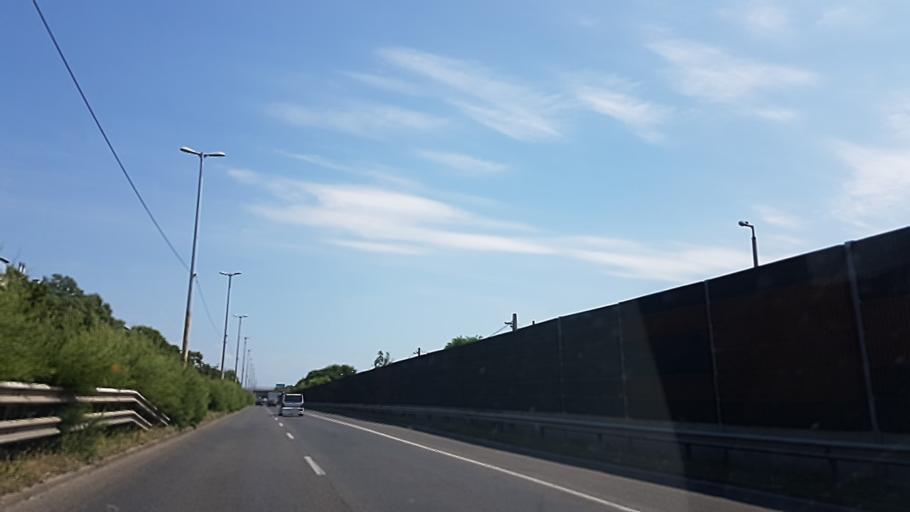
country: HU
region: Budapest
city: Budapest XX. keruelet
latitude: 47.4498
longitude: 19.1216
